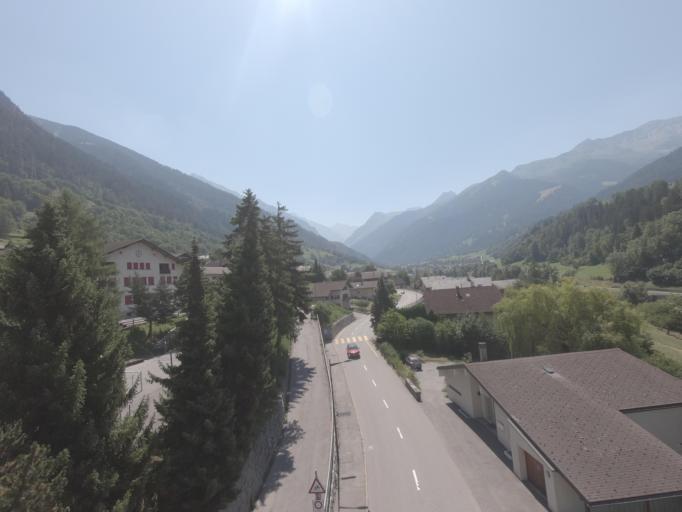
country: CH
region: Valais
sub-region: Entremont District
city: Bagnes
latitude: 46.0795
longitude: 7.2158
